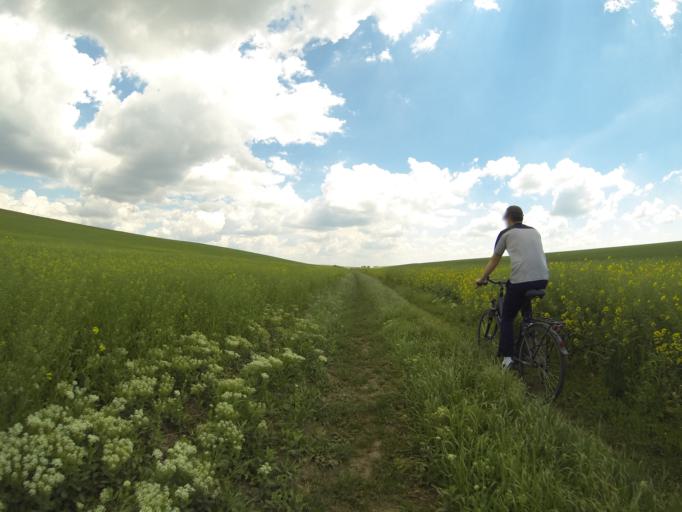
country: RO
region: Dolj
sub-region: Comuna Dranicu
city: Dranic
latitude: 44.0478
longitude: 23.8219
